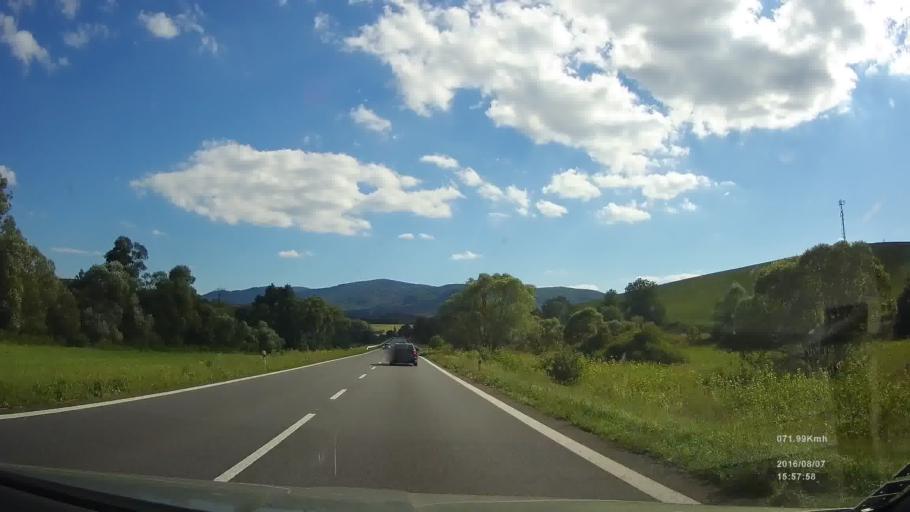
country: SK
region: Presovsky
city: Giraltovce
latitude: 49.0543
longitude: 21.4173
